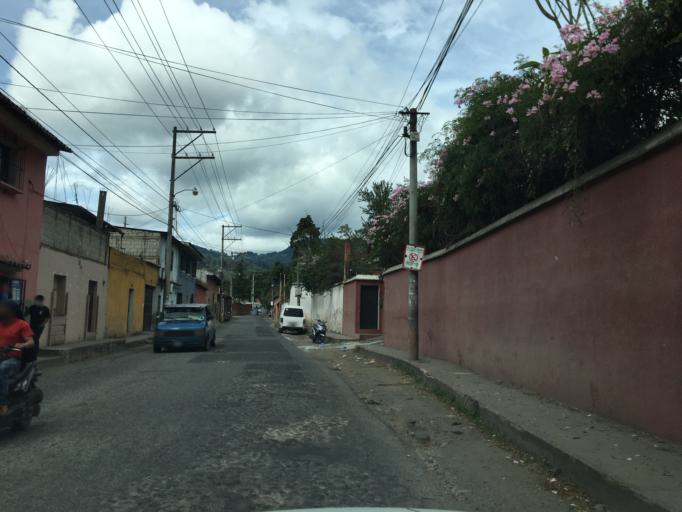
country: GT
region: Sacatepequez
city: Antigua Guatemala
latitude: 14.5560
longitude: -90.7265
